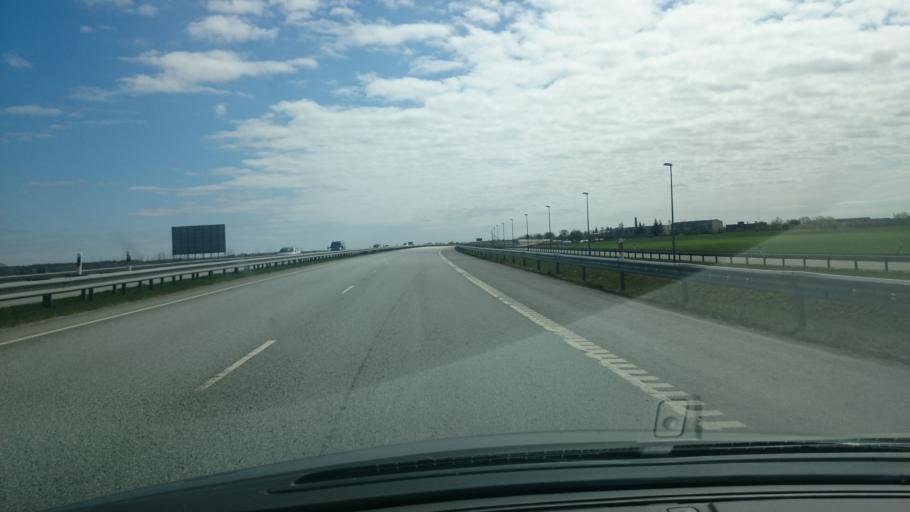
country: EE
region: Ida-Virumaa
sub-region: Johvi vald
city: Johvi
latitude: 59.3833
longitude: 27.3611
